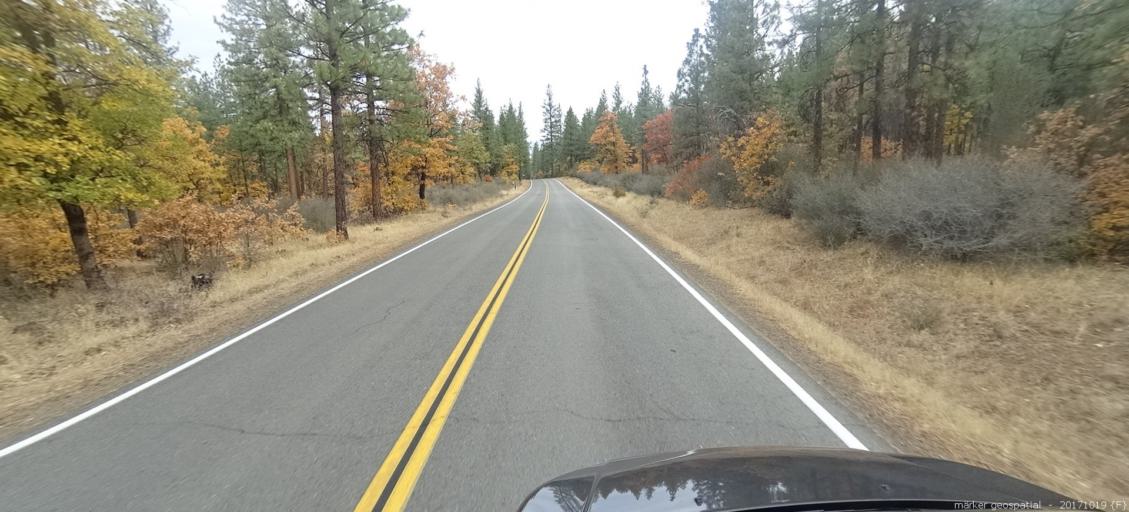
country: US
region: California
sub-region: Shasta County
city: Burney
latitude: 41.1757
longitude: -121.3619
